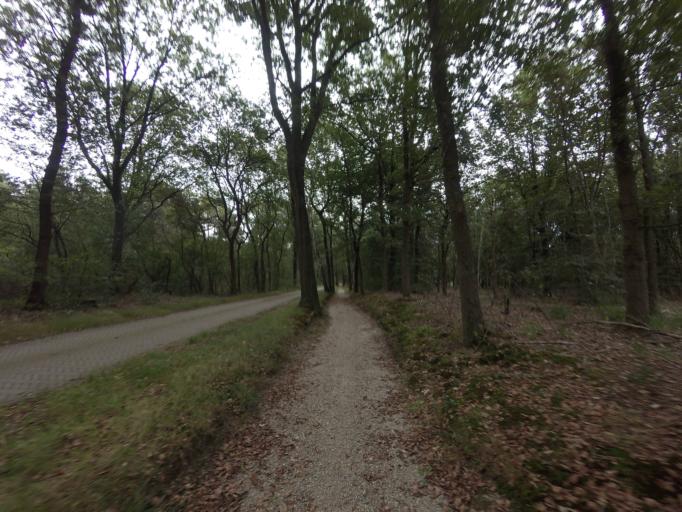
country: NL
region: Gelderland
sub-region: Gemeente Lochem
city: Laren
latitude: 52.2971
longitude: 6.3822
